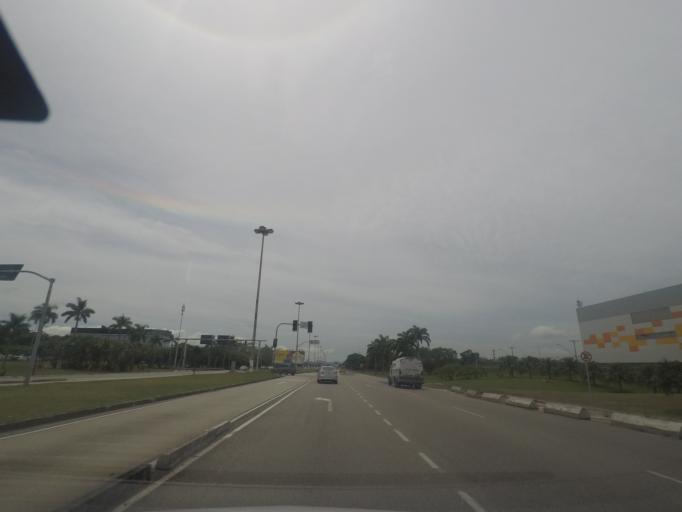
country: BR
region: Rio de Janeiro
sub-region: Duque De Caxias
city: Duque de Caxias
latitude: -22.8171
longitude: -43.2397
